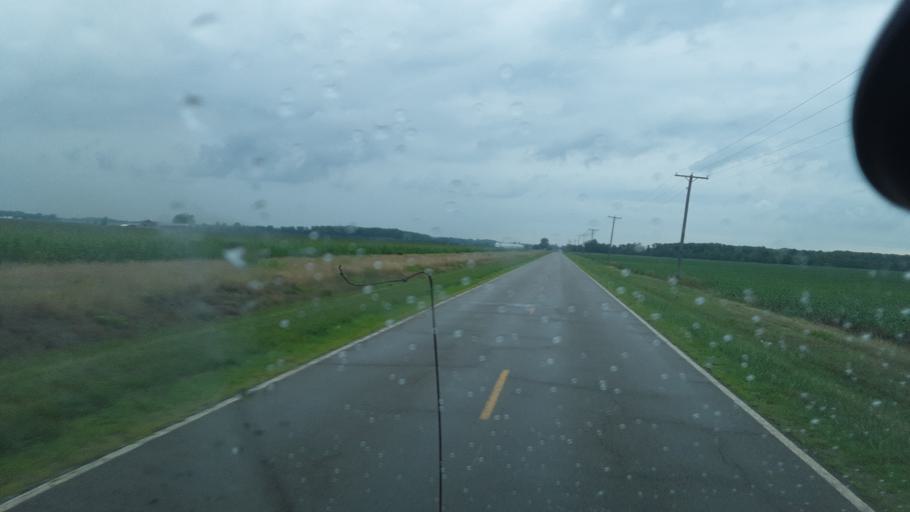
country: US
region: Ohio
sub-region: Defiance County
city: Hicksville
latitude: 41.3488
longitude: -84.6306
